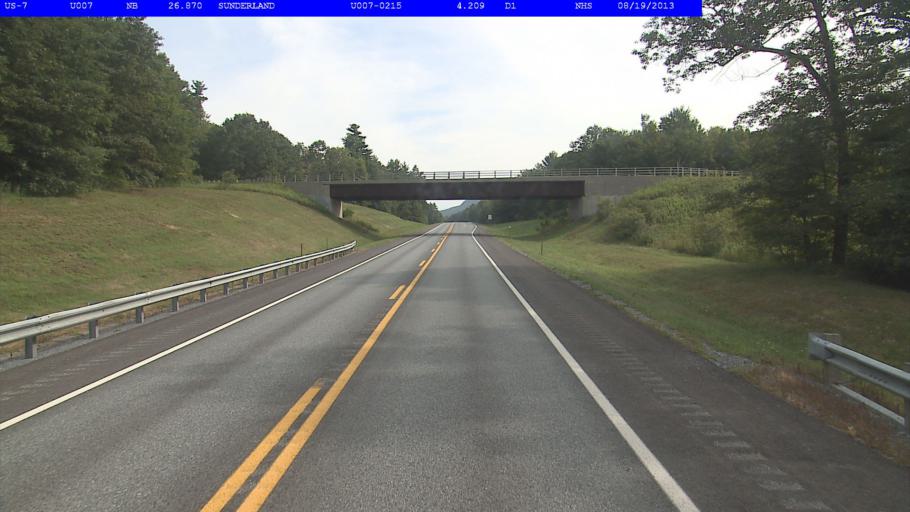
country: US
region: Vermont
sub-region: Bennington County
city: Arlington
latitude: 43.0823
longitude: -73.1115
